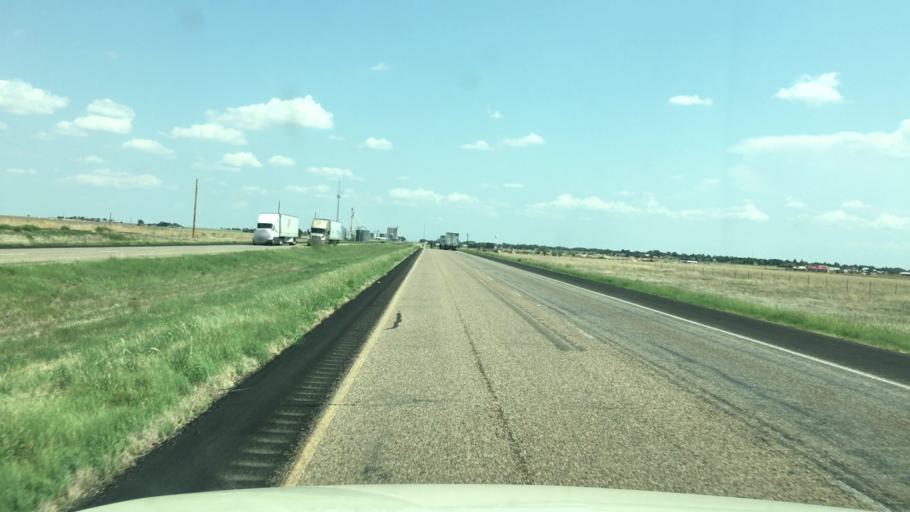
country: US
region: Texas
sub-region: Armstrong County
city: Claude
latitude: 35.1220
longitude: -101.3883
